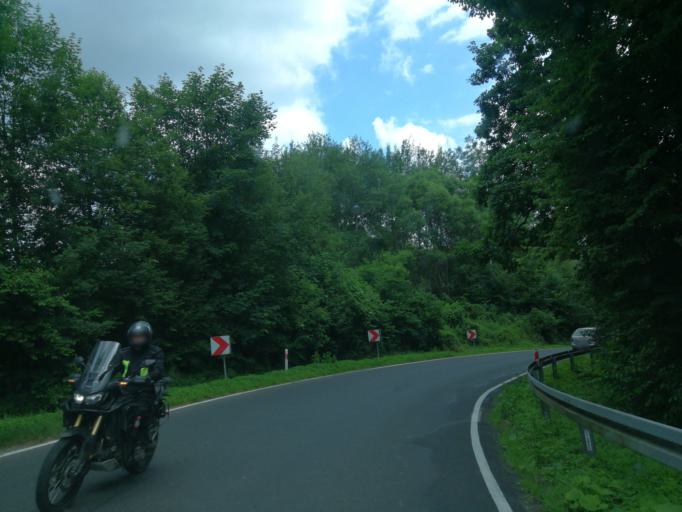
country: PL
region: Subcarpathian Voivodeship
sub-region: Powiat leski
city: Polanczyk
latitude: 49.4059
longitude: 22.4556
